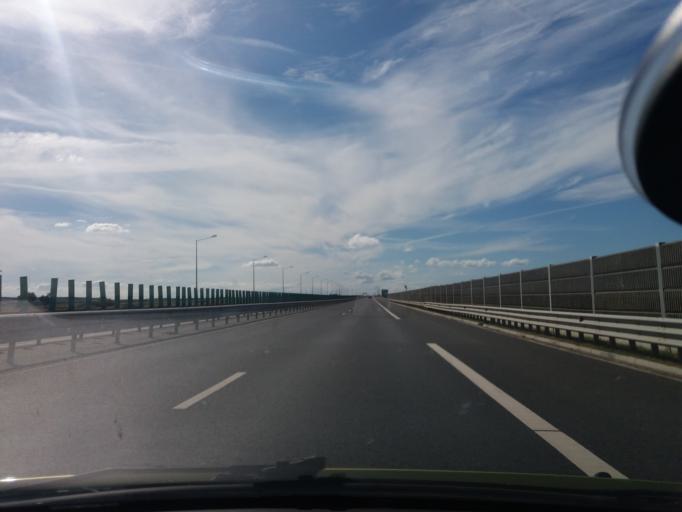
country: RO
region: Alba
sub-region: Comuna Pianu
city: Pianu de Jos
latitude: 45.9673
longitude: 23.4795
